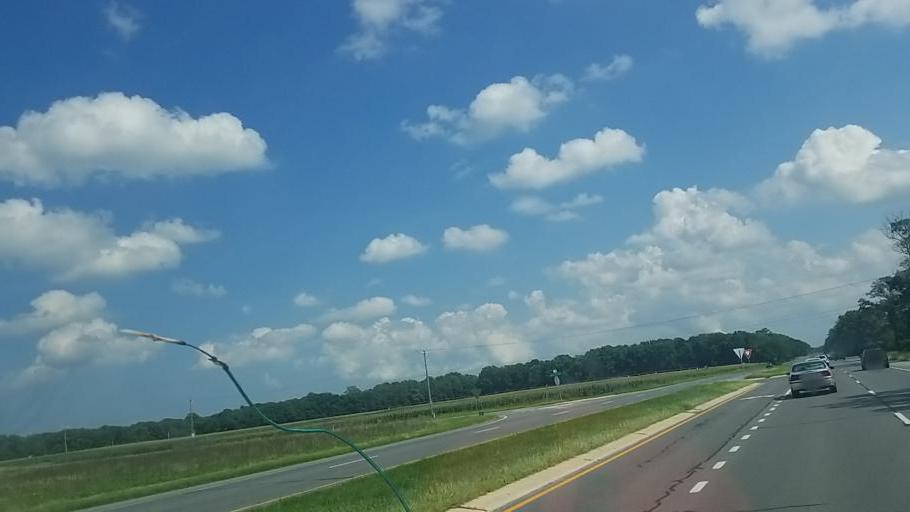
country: US
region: Delaware
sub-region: Sussex County
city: Millsboro
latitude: 38.6188
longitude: -75.3360
